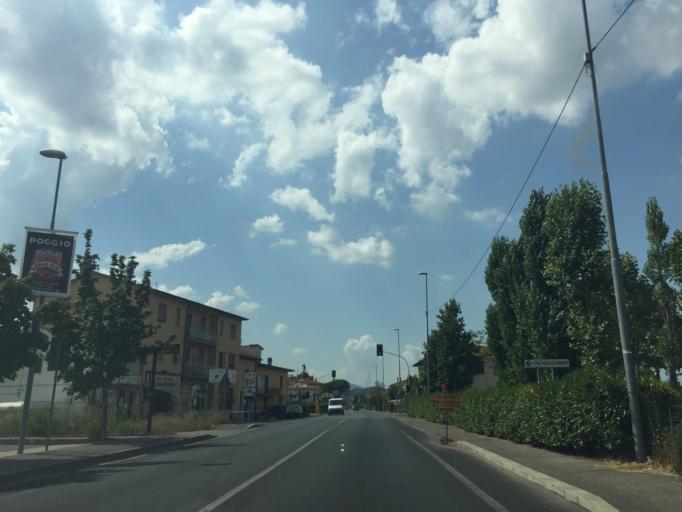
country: IT
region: Tuscany
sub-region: Province of Florence
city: Signa
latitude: 43.8107
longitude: 11.0834
